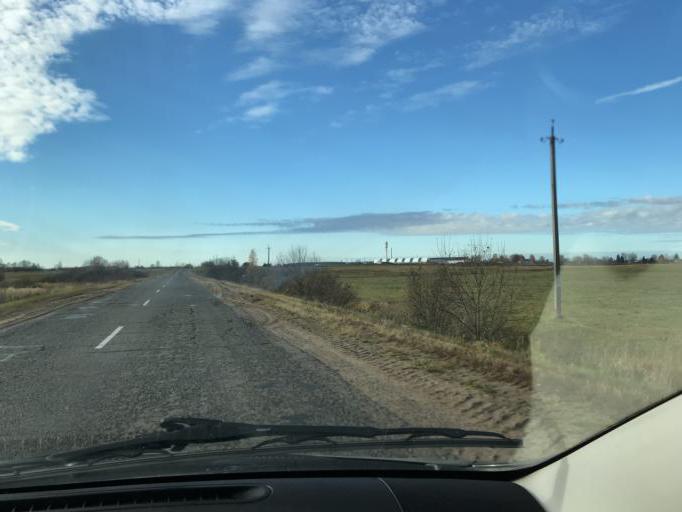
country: BY
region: Vitebsk
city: Haradok
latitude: 55.3787
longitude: 29.6434
